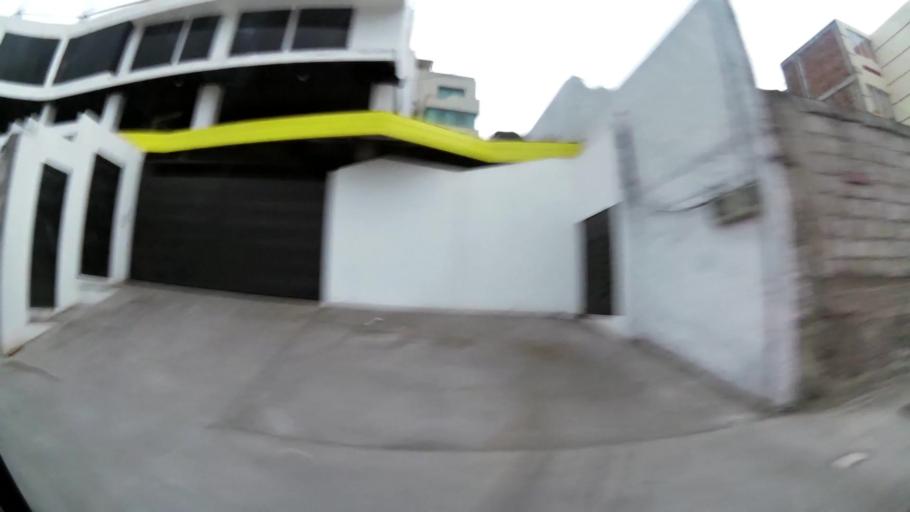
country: EC
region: Tungurahua
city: Ambato
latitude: -1.2557
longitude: -78.6419
